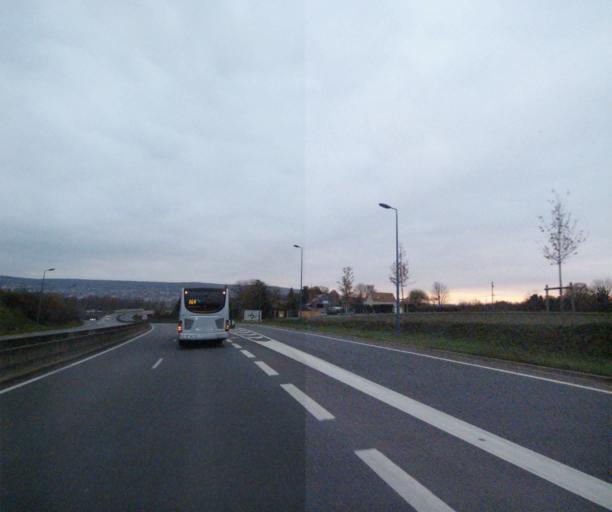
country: FR
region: Ile-de-France
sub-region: Departement des Yvelines
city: Medan
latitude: 48.9629
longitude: 1.9885
